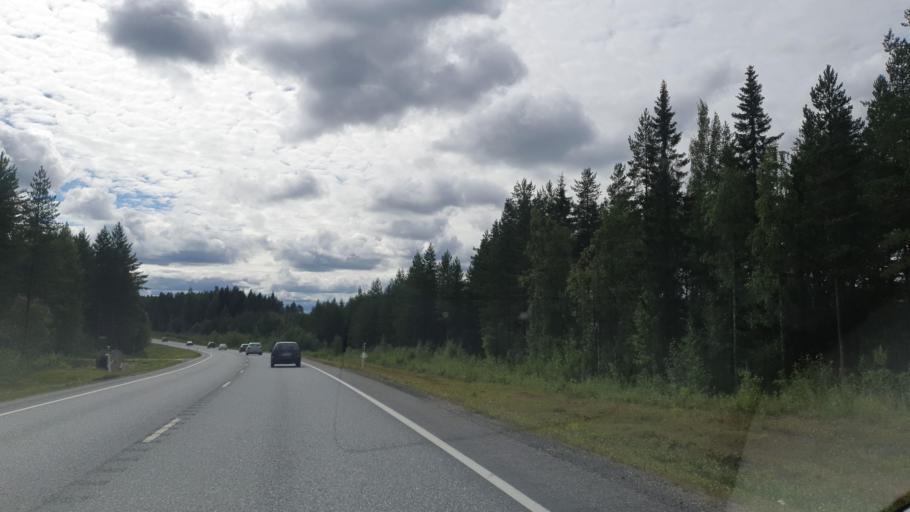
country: FI
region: Kainuu
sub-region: Kajaani
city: Kajaani
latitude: 64.1679
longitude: 27.5327
